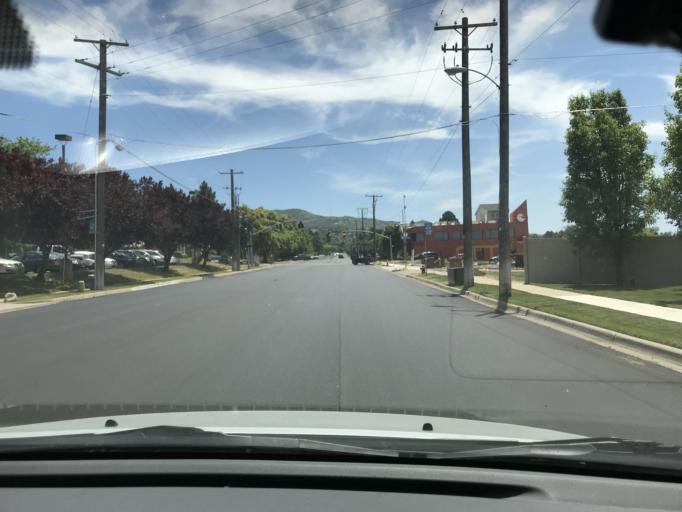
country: US
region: Utah
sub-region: Davis County
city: Woods Cross
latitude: 40.8624
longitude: -111.8923
